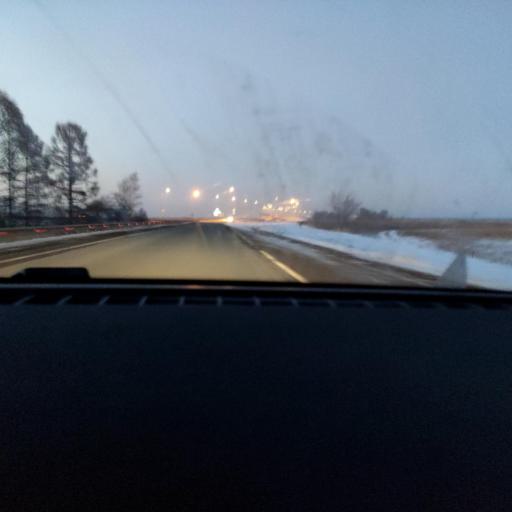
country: RU
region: Samara
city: Bereza
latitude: 53.4916
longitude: 50.1188
